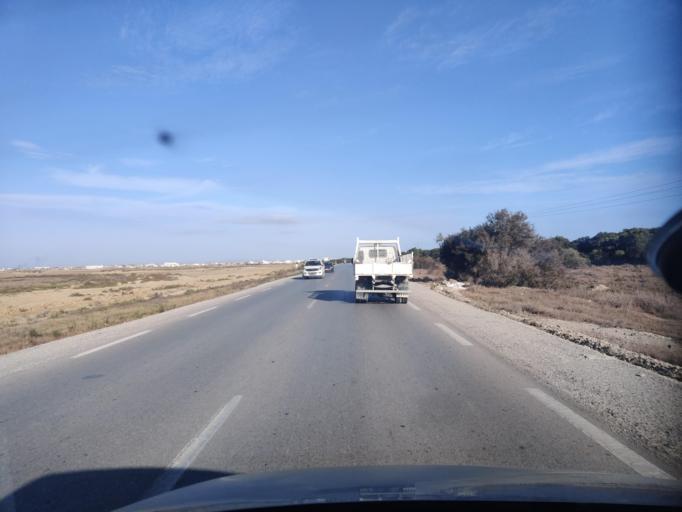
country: TN
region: Ariana
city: Ariana
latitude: 36.9443
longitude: 10.2448
